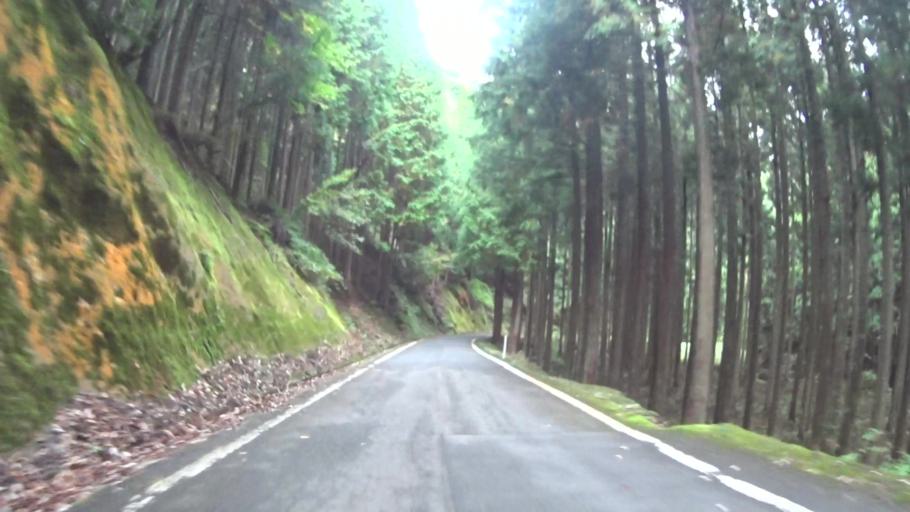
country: JP
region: Fukui
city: Obama
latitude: 35.2778
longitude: 135.6982
